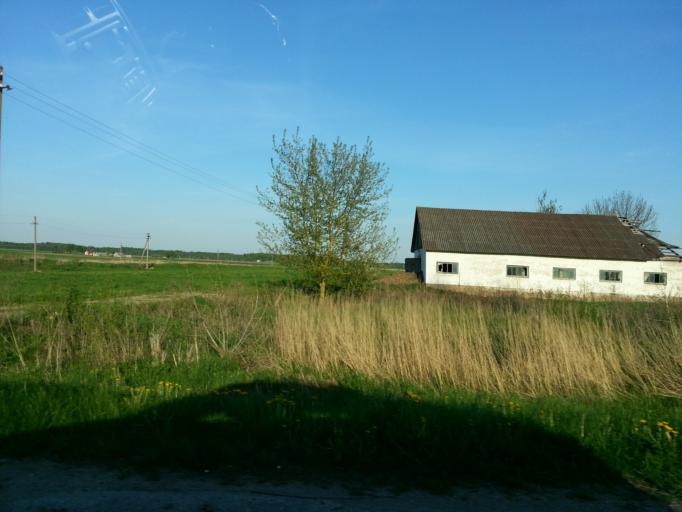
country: LT
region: Vilnius County
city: Ukmerge
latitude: 55.4224
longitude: 24.5851
